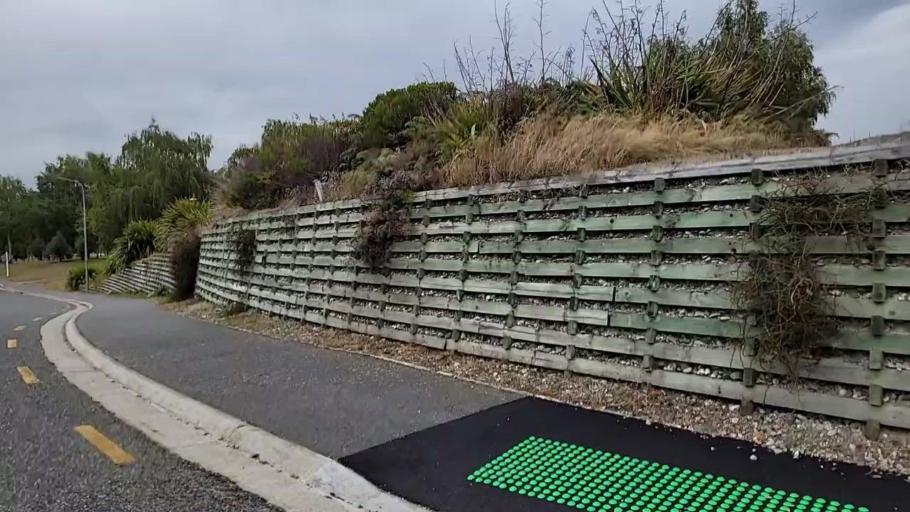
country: NZ
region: Otago
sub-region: Queenstown-Lakes District
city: Wanaka
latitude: -45.0396
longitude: 169.2093
